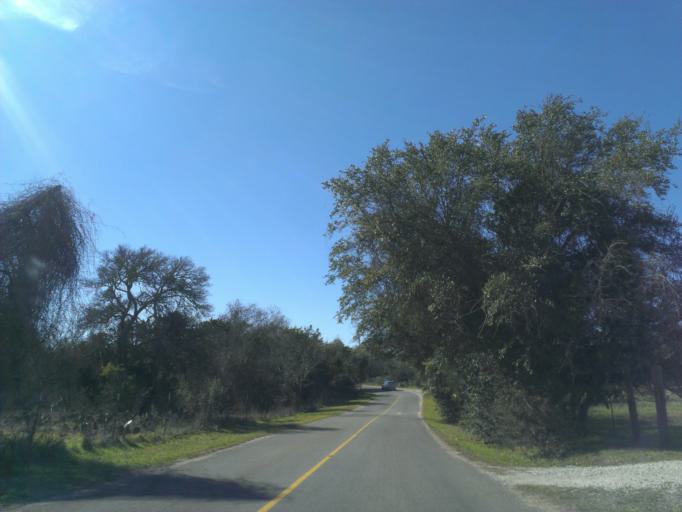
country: US
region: Texas
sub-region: Travis County
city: Briarcliff
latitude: 30.4688
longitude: -98.1158
